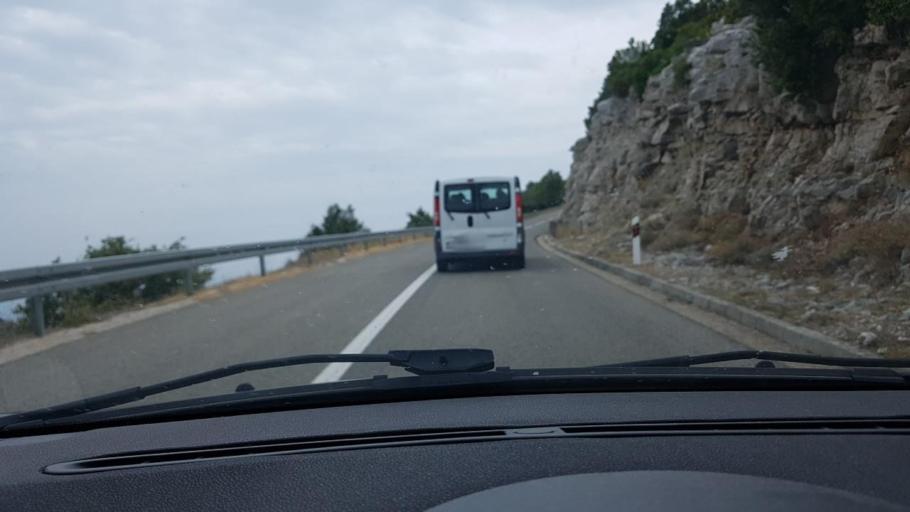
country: HR
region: Dubrovacko-Neretvanska
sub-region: Grad Korcula
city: Zrnovo
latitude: 42.9406
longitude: 17.0244
